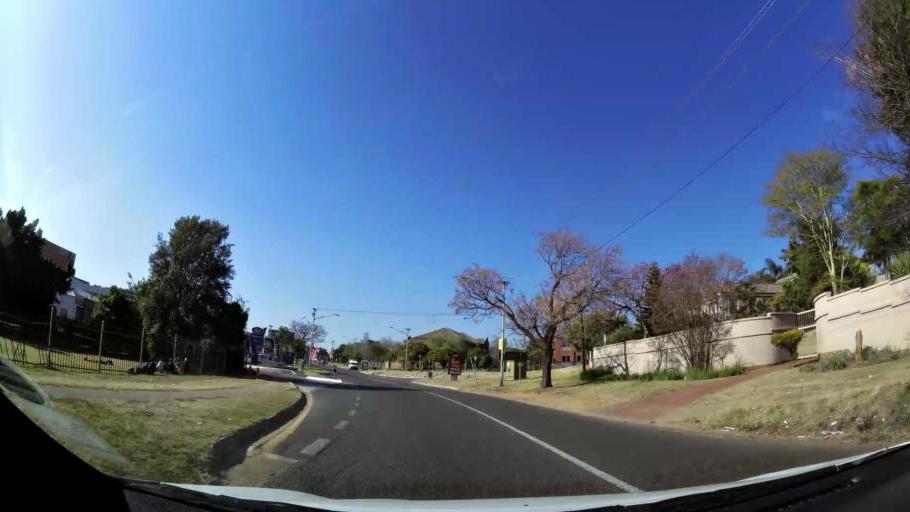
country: ZA
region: Gauteng
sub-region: City of Tshwane Metropolitan Municipality
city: Centurion
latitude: -25.8090
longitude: 28.2543
